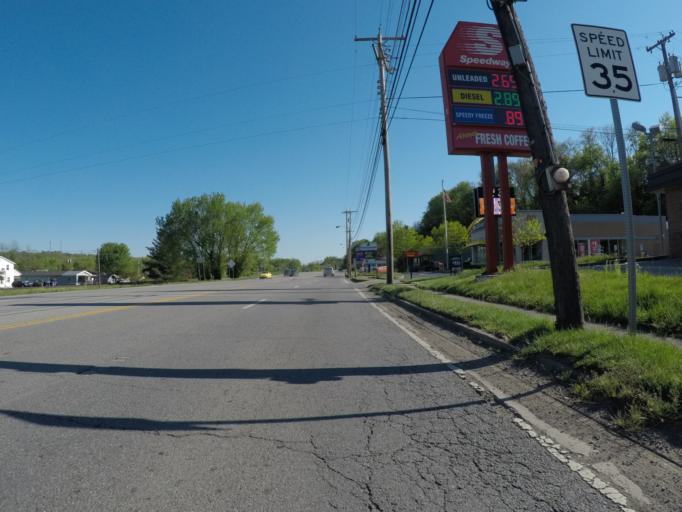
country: US
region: Kentucky
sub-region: Boyd County
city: Catlettsburg
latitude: 38.4029
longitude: -82.6010
